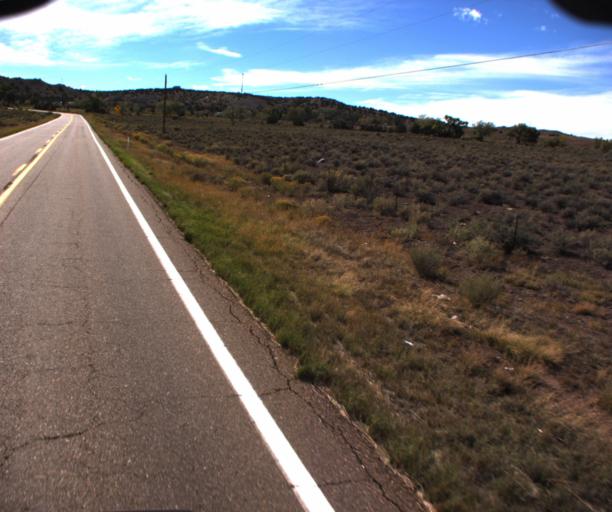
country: US
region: Arizona
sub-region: Apache County
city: Saint Johns
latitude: 34.4693
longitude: -109.6141
